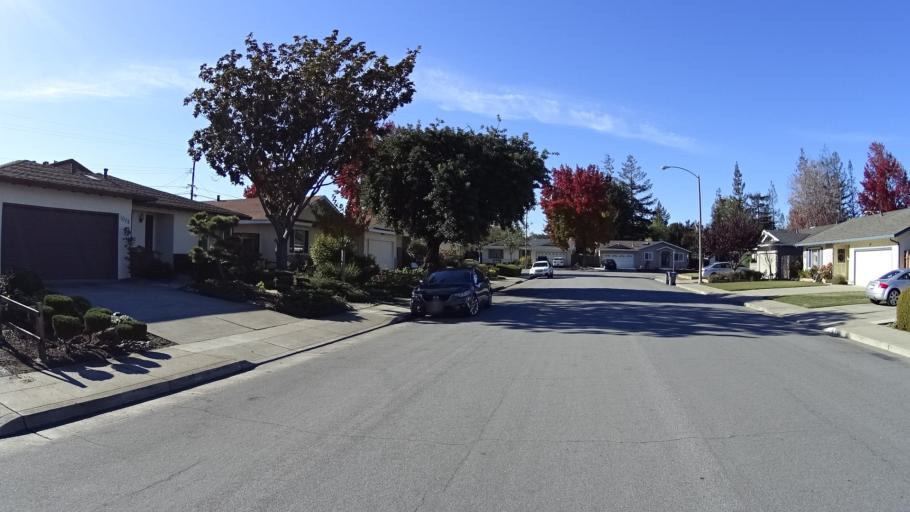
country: US
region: California
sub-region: Santa Clara County
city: Sunnyvale
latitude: 37.3585
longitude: -122.0078
